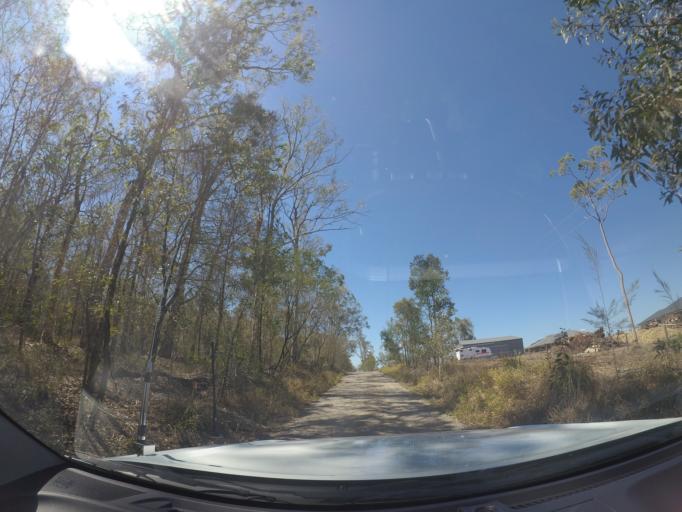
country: AU
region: Queensland
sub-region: Logan
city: North Maclean
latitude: -27.7565
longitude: 152.9419
